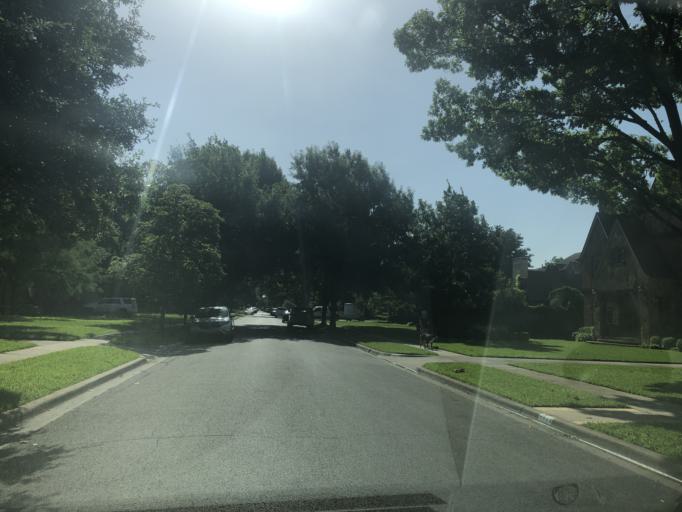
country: US
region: Texas
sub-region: Dallas County
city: University Park
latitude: 32.8570
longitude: -96.8114
